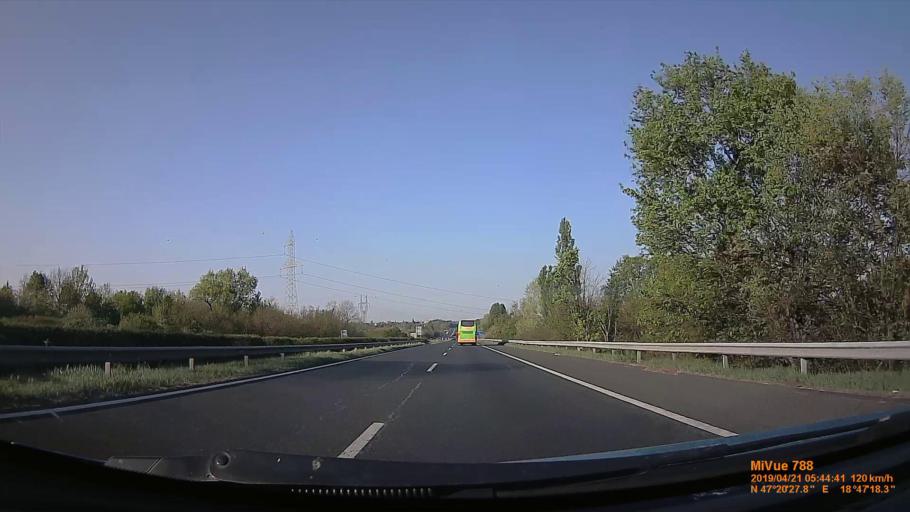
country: HU
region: Fejer
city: Martonvasar
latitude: 47.3409
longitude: 18.7876
